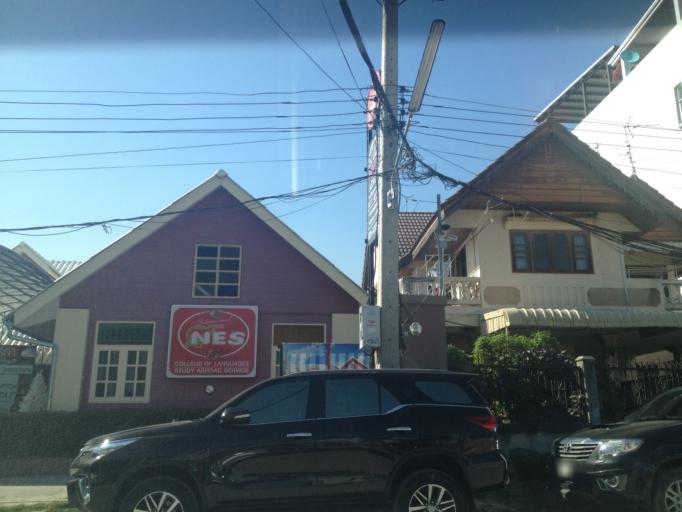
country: TH
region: Chiang Mai
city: Chiang Mai
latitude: 18.7949
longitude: 98.9667
